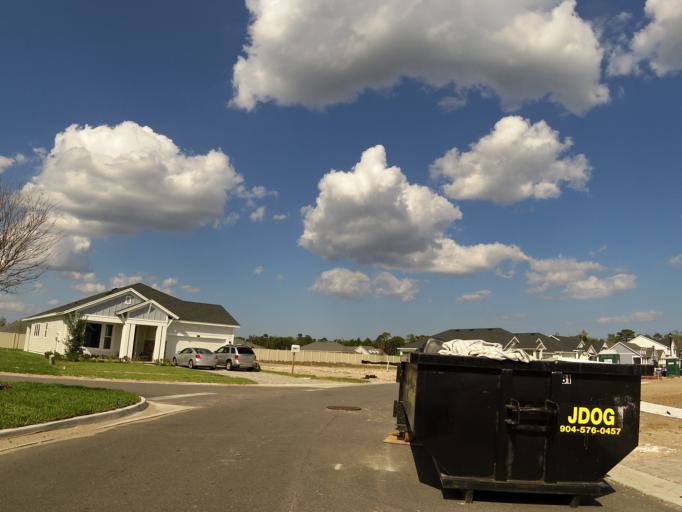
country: US
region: Florida
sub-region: Saint Johns County
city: Palm Valley
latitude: 30.1753
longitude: -81.5052
